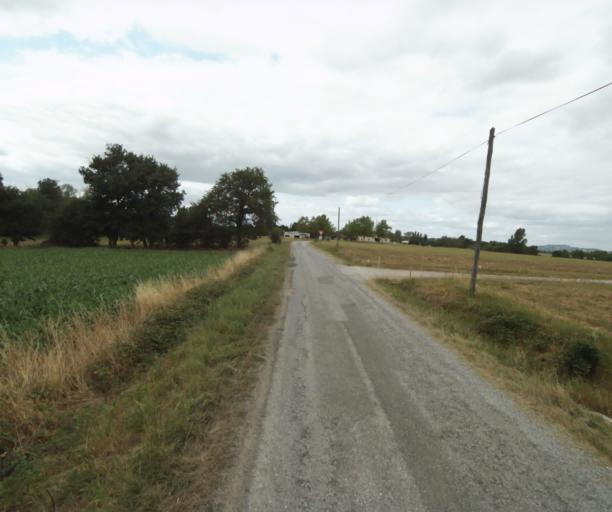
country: FR
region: Midi-Pyrenees
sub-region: Departement de la Haute-Garonne
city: Revel
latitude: 43.4833
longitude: 2.0292
